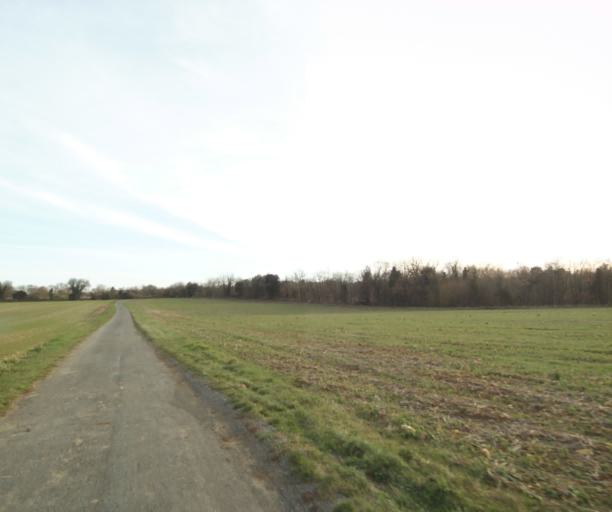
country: FR
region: Poitou-Charentes
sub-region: Departement de la Charente-Maritime
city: Saint-Hilaire-de-Villefranche
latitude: 45.8252
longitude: -0.5713
